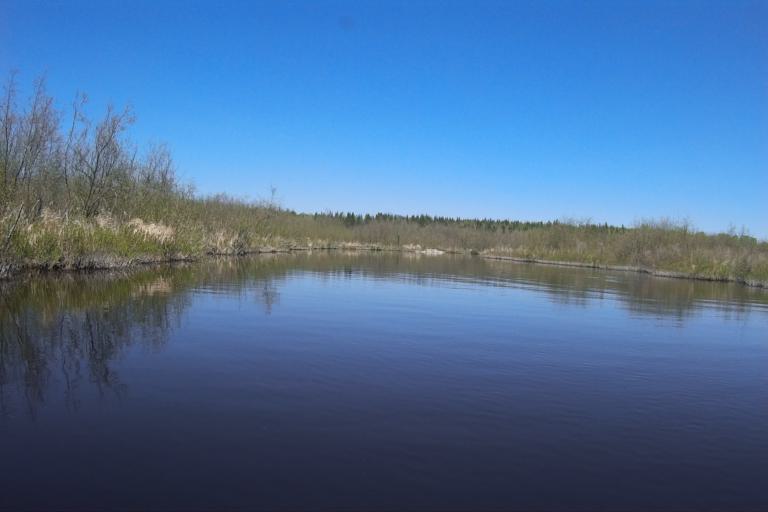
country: CA
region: Ontario
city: Powassan
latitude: 46.1582
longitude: -79.2537
